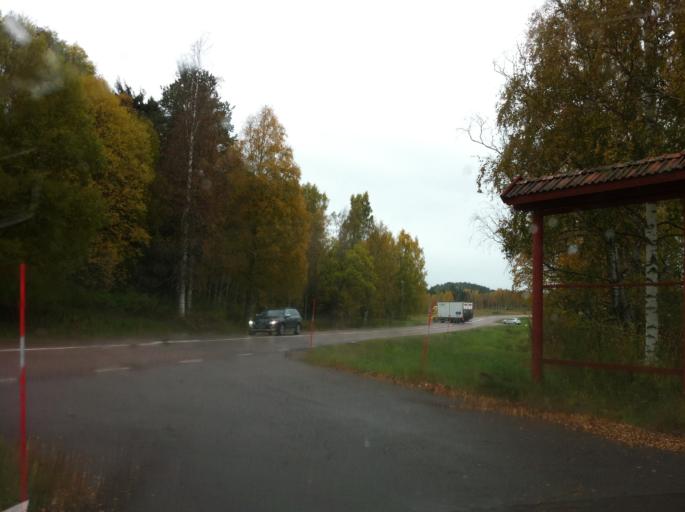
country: SE
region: Dalarna
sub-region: Ludvika Kommun
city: Grangesberg
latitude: 60.2137
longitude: 14.9576
